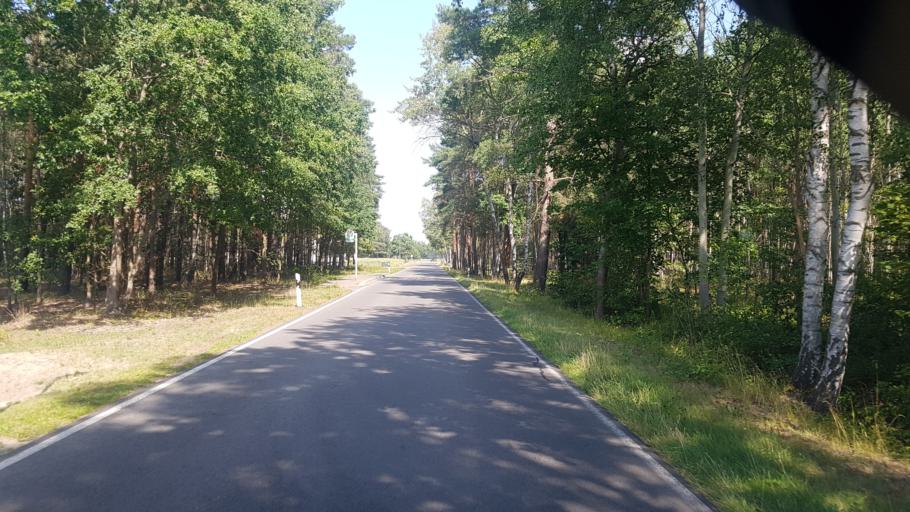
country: DE
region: Brandenburg
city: Cottbus
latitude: 51.6897
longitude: 14.4181
